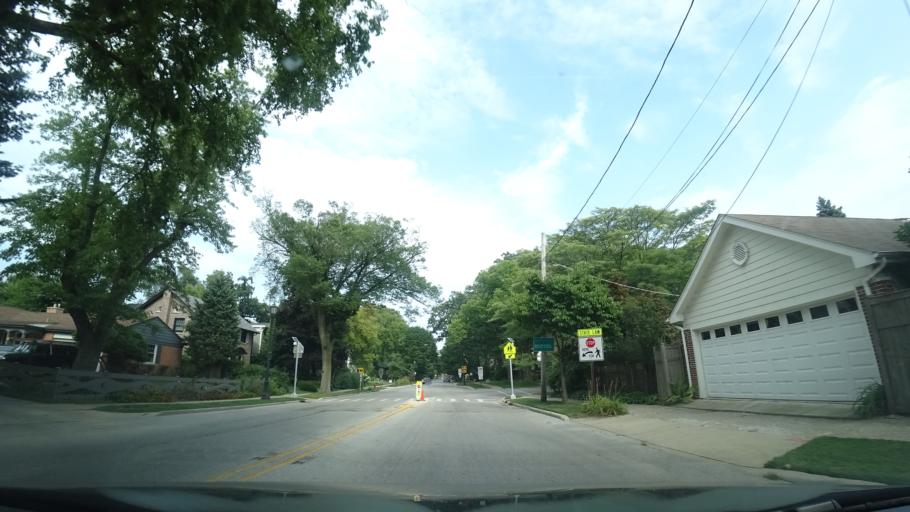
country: US
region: Illinois
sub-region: Cook County
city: Evanston
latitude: 42.0640
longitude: -87.6821
